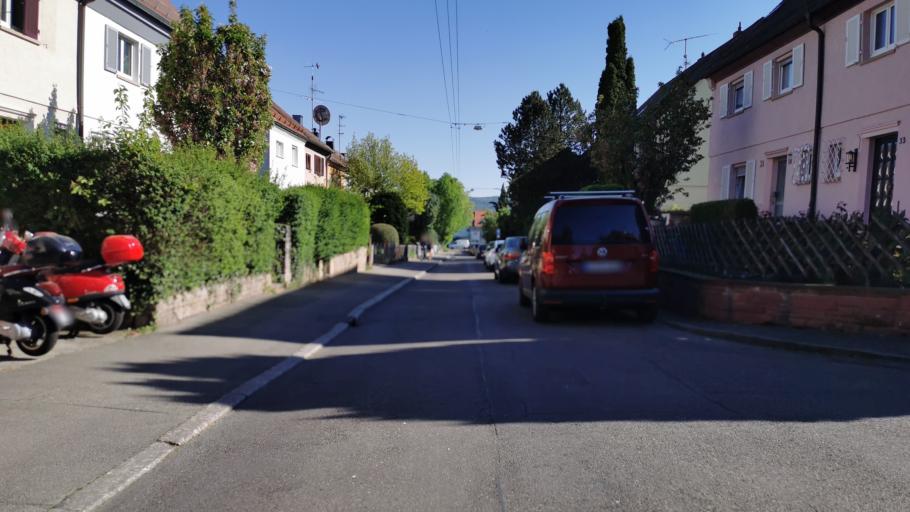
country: DE
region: Baden-Wuerttemberg
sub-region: Regierungsbezirk Stuttgart
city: Stuttgart-Ost
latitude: 48.8119
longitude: 9.2056
